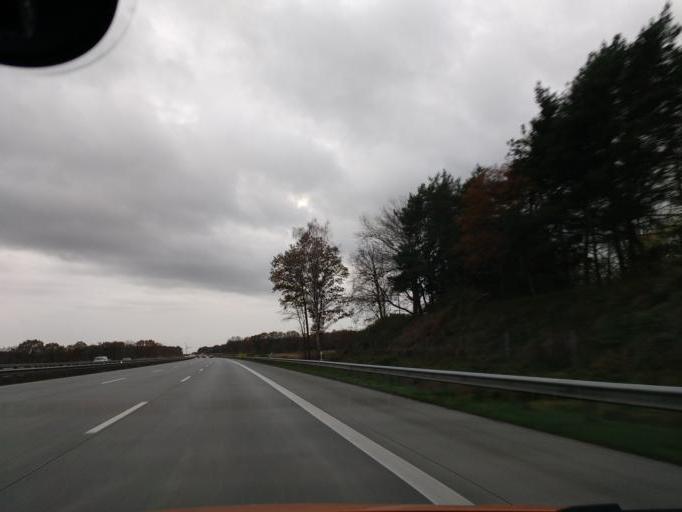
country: DE
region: Lower Saxony
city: Horstedt
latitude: 53.1690
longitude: 9.2496
